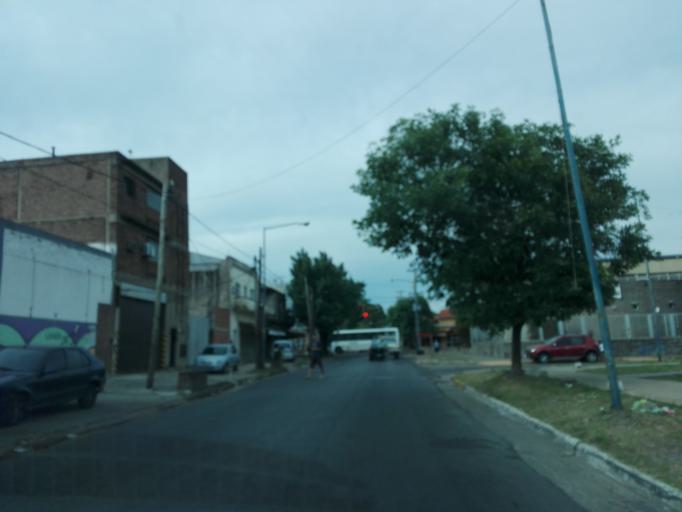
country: AR
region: Buenos Aires
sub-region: Partido de Lanus
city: Lanus
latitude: -34.7021
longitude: -58.3654
